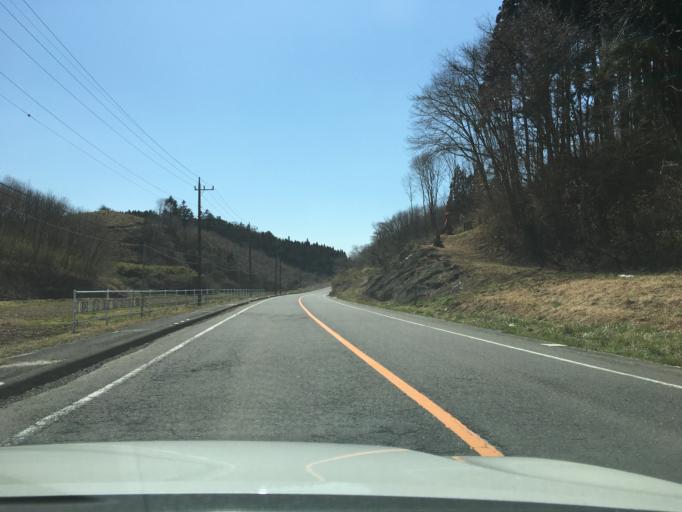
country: JP
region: Tochigi
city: Kuroiso
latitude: 37.0660
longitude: 140.1828
